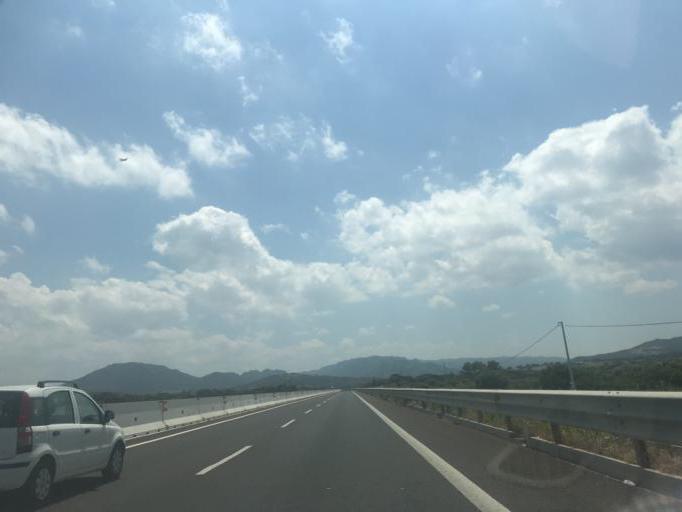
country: IT
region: Sardinia
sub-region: Provincia di Olbia-Tempio
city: Loiri Porto San Paolo
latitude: 40.8744
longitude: 9.4611
